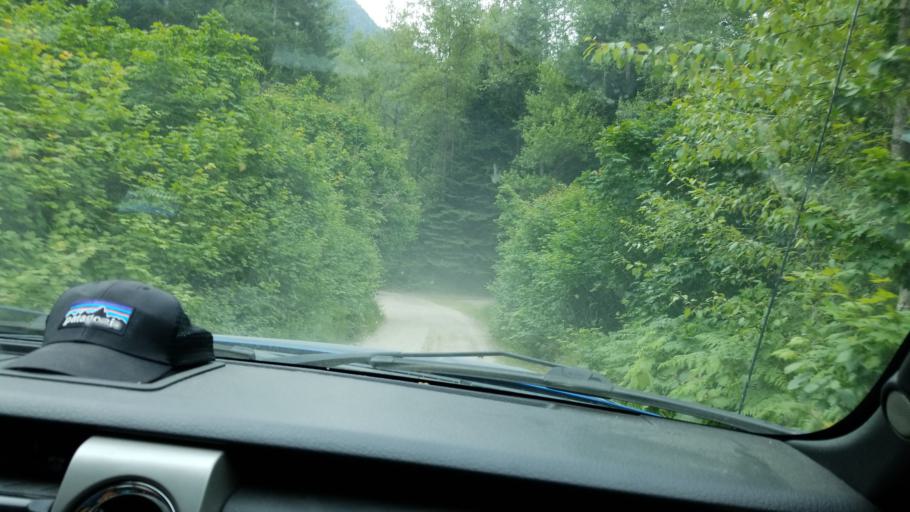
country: US
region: Washington
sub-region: Chelan County
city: Leavenworth
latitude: 47.9236
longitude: -120.9015
